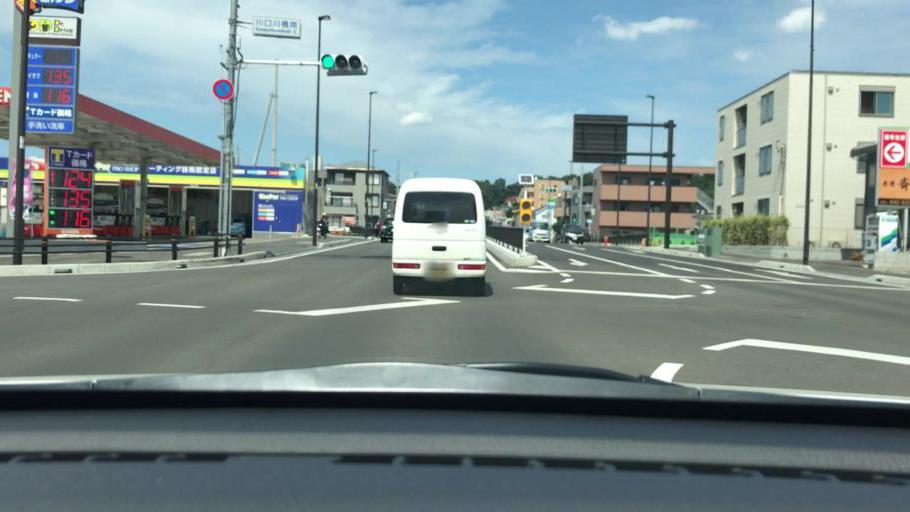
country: JP
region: Tokyo
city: Hachioji
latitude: 35.6683
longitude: 139.3307
